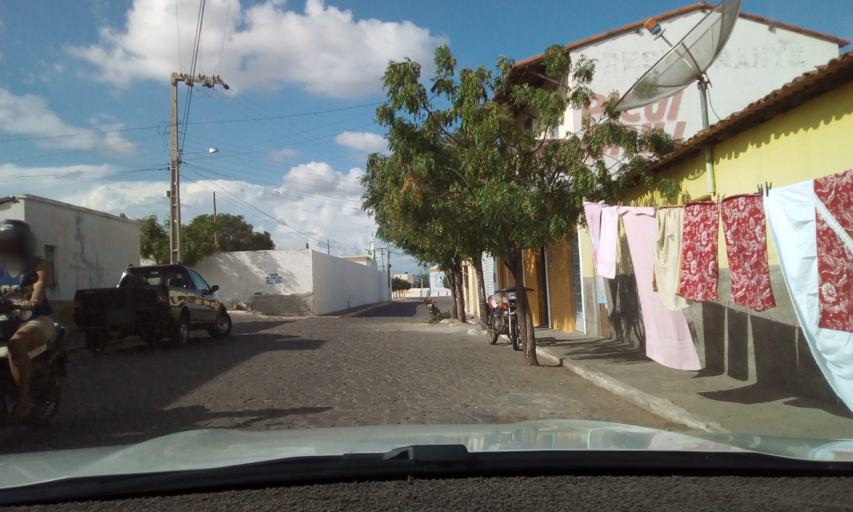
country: BR
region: Paraiba
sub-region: Picui
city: Picui
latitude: -6.5104
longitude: -36.3511
